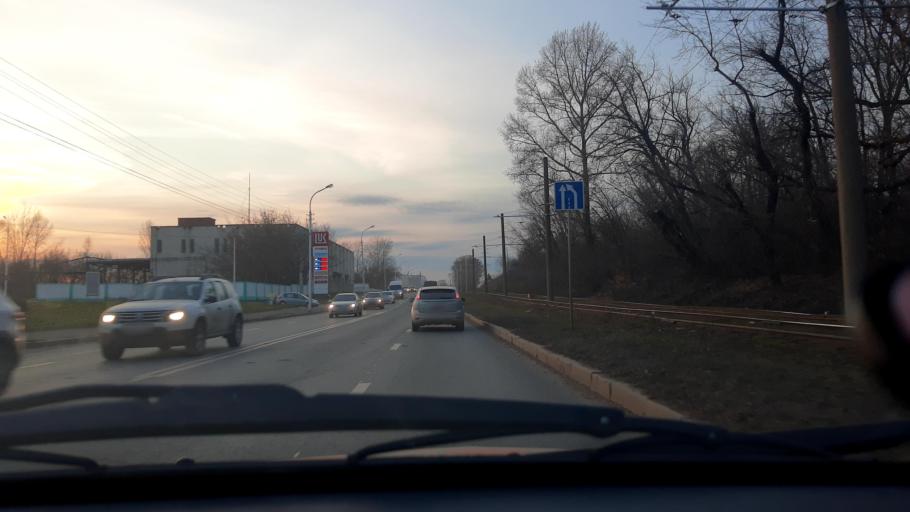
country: RU
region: Bashkortostan
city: Ufa
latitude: 54.7983
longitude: 56.1210
